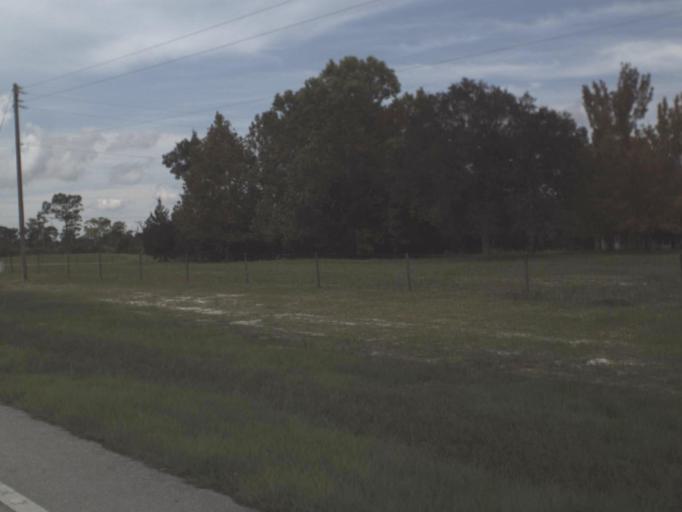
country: US
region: Florida
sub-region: Highlands County
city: Placid Lakes
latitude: 27.2098
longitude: -81.3556
